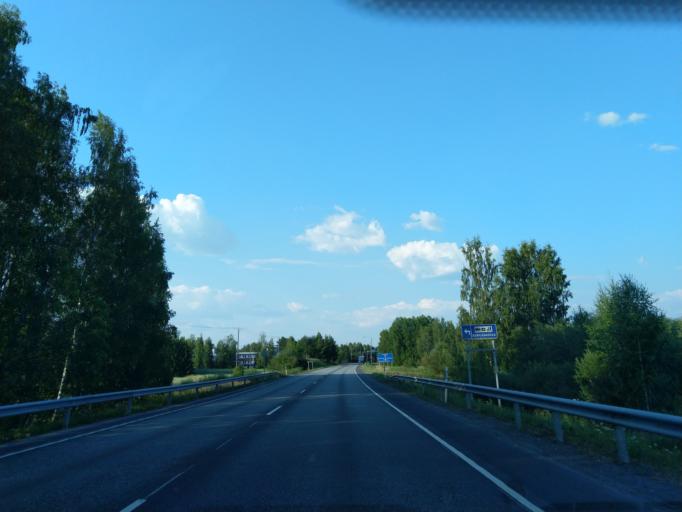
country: FI
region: Satakunta
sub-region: Pori
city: Pomarkku
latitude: 61.6964
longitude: 22.0061
